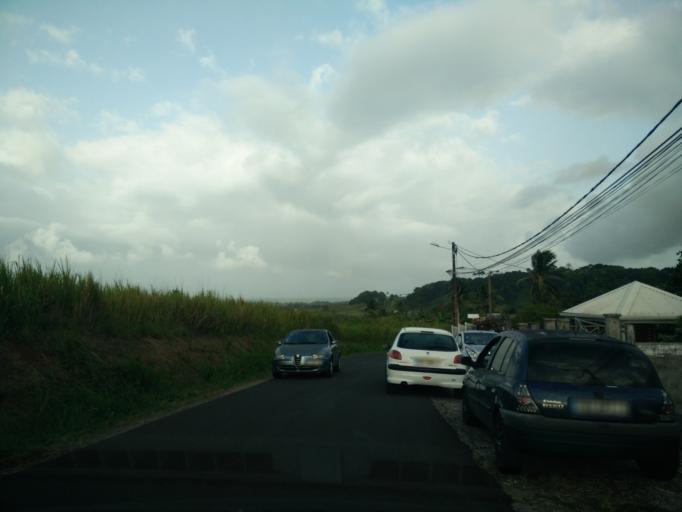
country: GP
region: Guadeloupe
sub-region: Guadeloupe
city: Petit-Bourg
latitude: 16.1833
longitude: -61.6095
